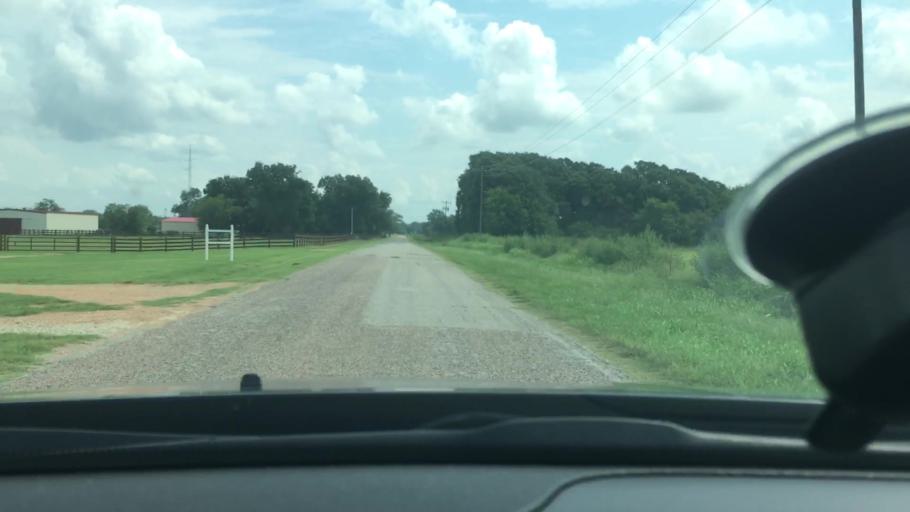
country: US
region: Oklahoma
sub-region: Carter County
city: Dickson
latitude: 34.2271
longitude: -96.8966
